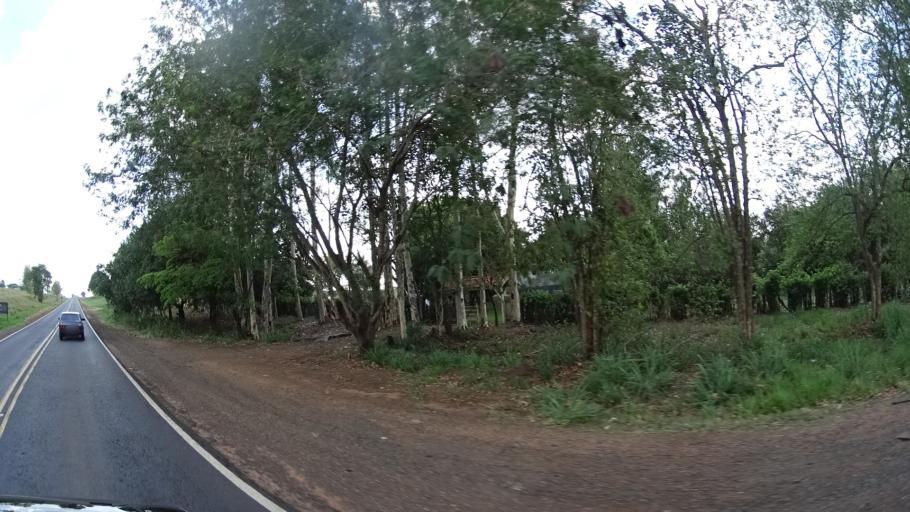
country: BR
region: Sao Paulo
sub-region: Urupes
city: Urupes
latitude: -21.1338
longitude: -49.2772
